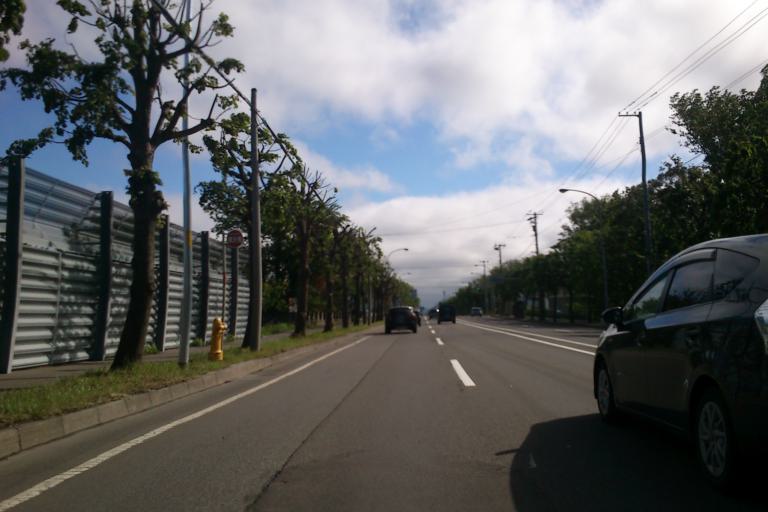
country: JP
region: Hokkaido
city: Sapporo
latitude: 43.1394
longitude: 141.2714
